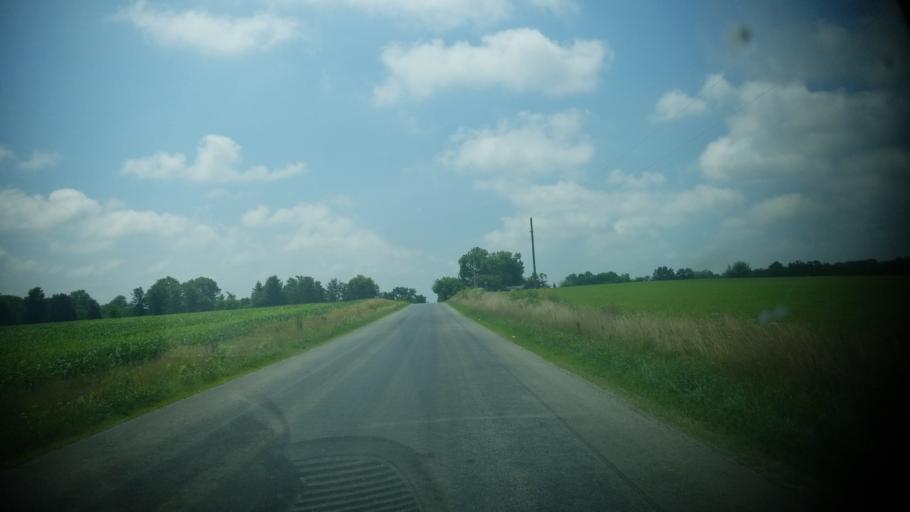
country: US
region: Illinois
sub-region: Wayne County
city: Fairfield
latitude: 38.5176
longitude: -88.3485
